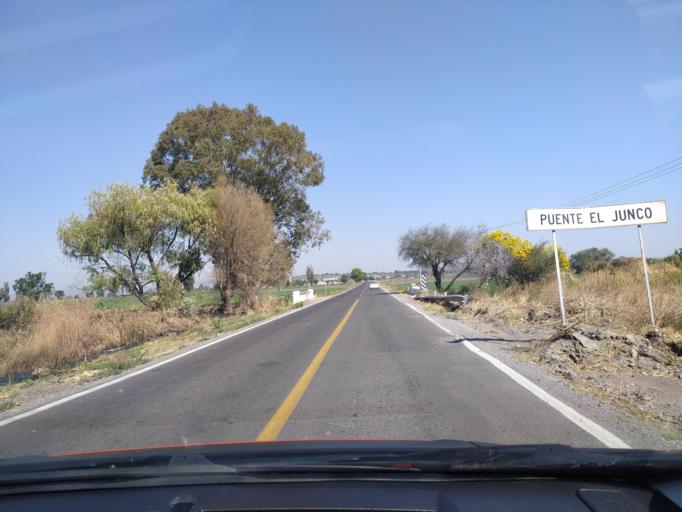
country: MX
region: Guanajuato
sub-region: San Francisco del Rincon
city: San Ignacio de Hidalgo
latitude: 20.8391
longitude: -101.8467
